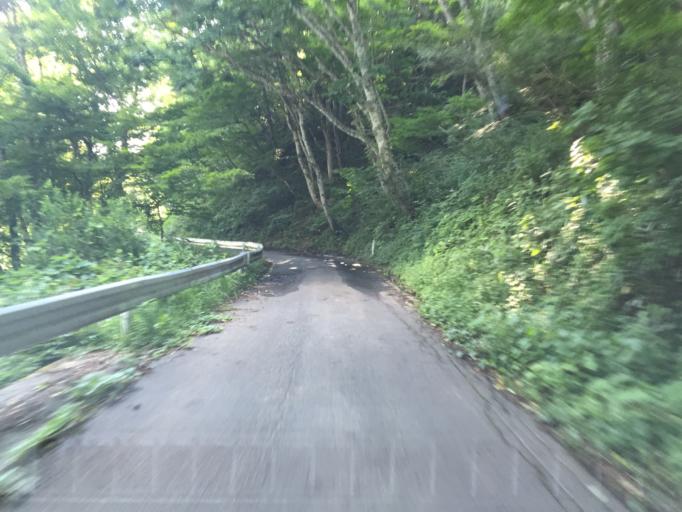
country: JP
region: Yamagata
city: Takahata
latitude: 37.9674
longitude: 140.3296
